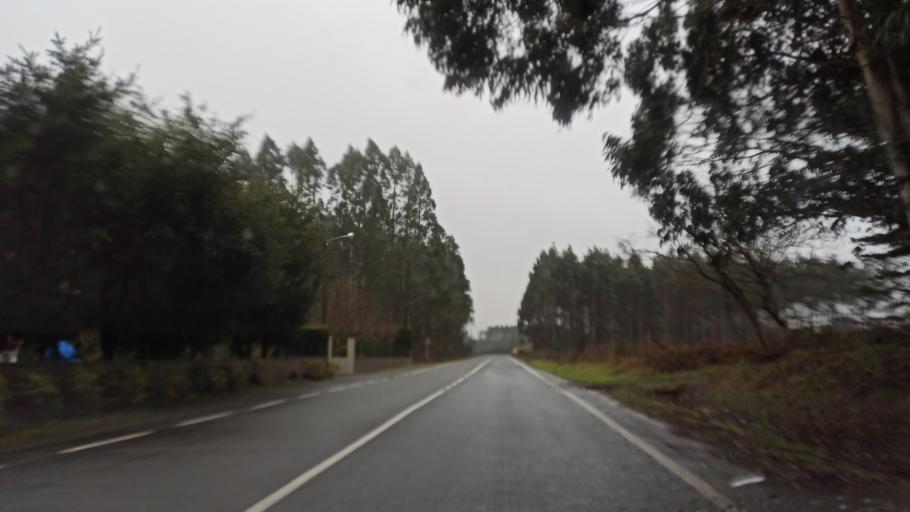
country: ES
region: Galicia
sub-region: Provincia da Coruna
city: Coiros
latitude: 43.1827
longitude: -8.1232
